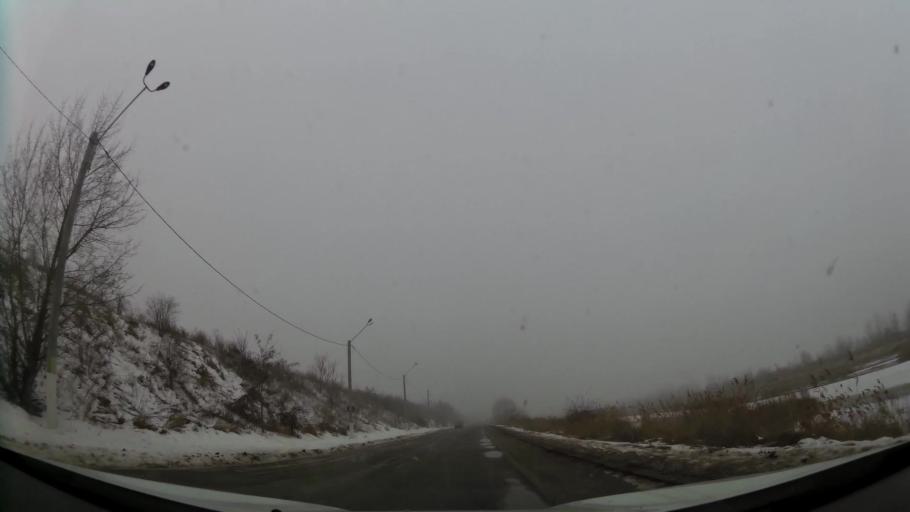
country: RO
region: Ilfov
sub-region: Comuna Chiajna
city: Chiajna
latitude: 44.4643
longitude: 25.9883
